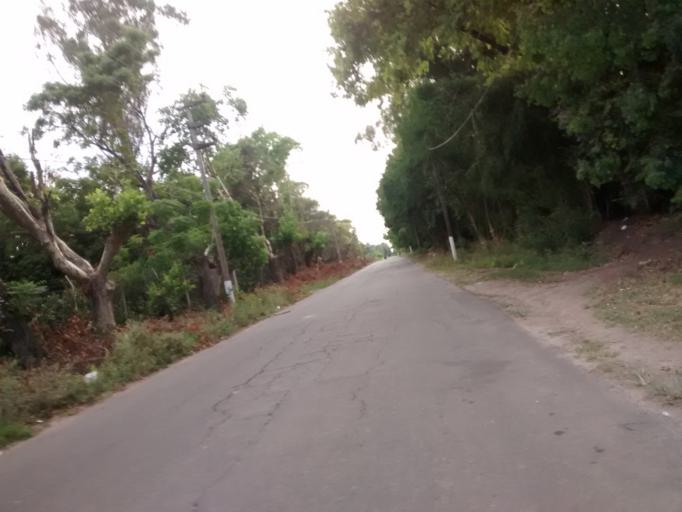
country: AR
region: Buenos Aires
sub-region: Partido de La Plata
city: La Plata
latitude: -34.8421
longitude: -58.0924
